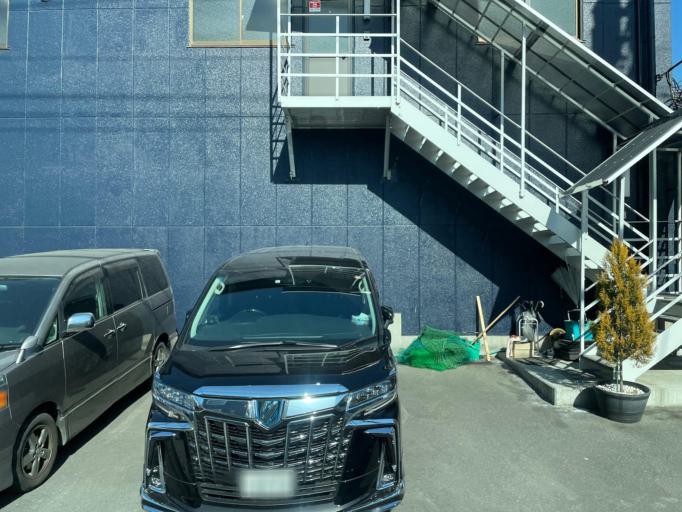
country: JP
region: Tokyo
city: Fussa
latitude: 35.7724
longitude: 139.3503
